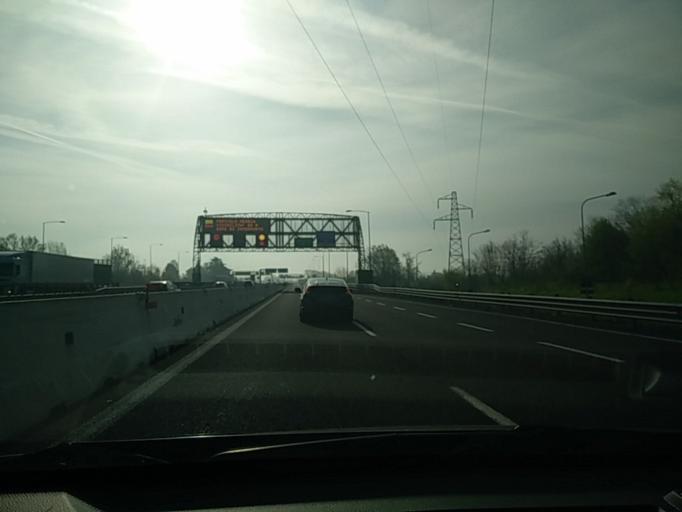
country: IT
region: Emilia-Romagna
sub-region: Provincia di Bologna
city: San Lazzaro
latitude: 44.4835
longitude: 11.4132
